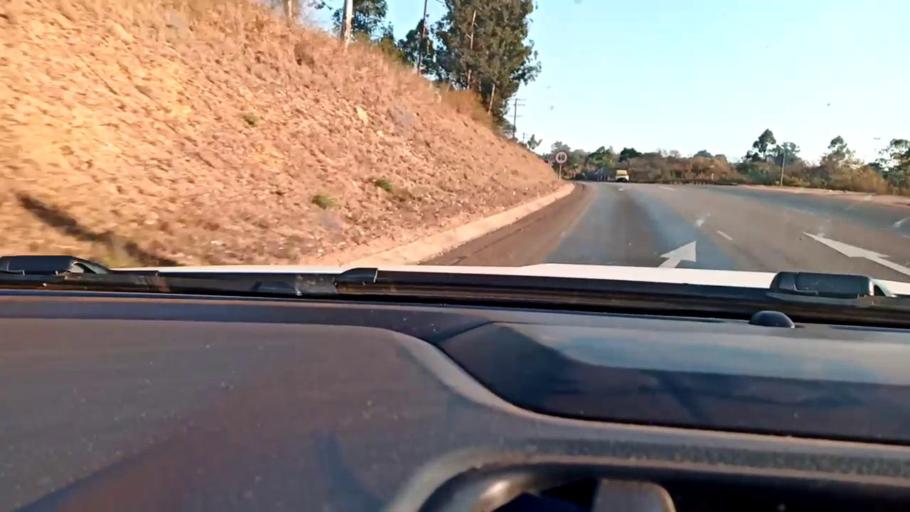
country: ZA
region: Limpopo
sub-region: Mopani District Municipality
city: Duiwelskloof
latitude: -23.6872
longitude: 30.1479
